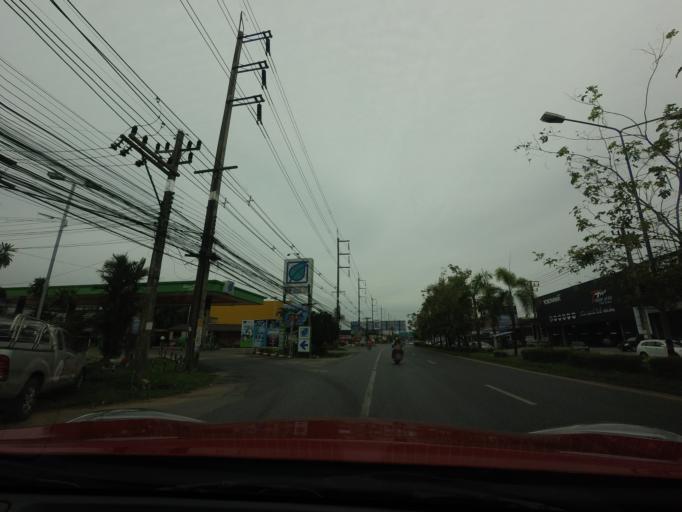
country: TH
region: Songkhla
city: Hat Yai
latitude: 6.9803
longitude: 100.4793
